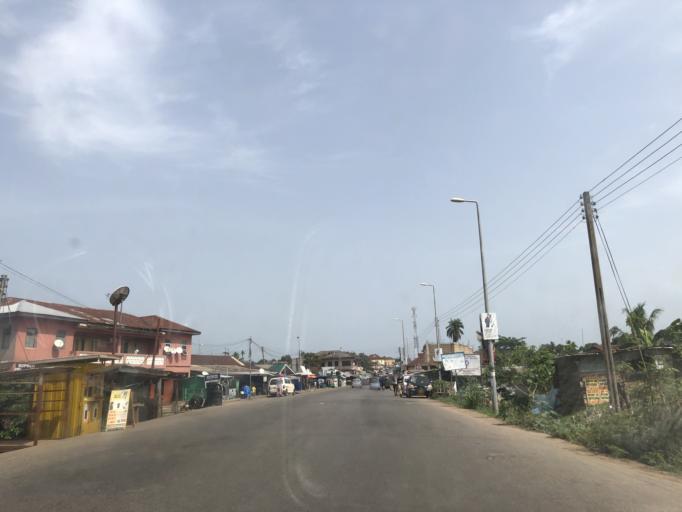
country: GH
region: Eastern
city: Koforidua
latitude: 6.0973
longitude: -0.2621
